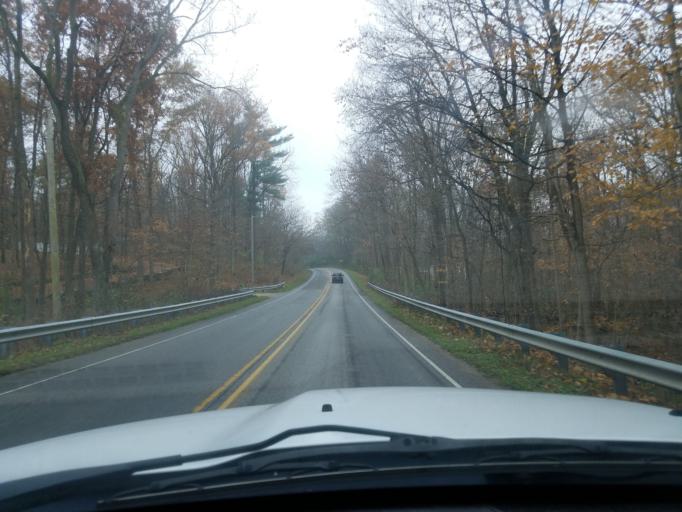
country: US
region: Indiana
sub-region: Cass County
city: Walton
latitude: 40.7658
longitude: -86.2511
